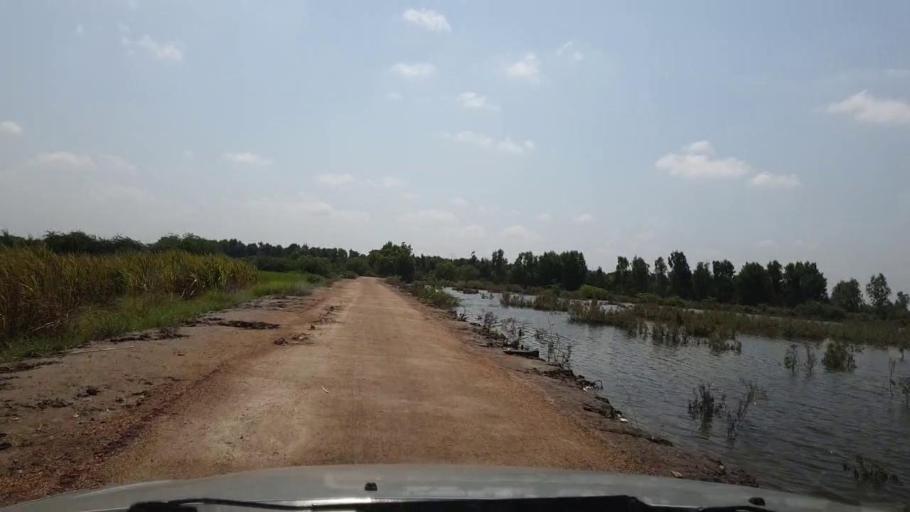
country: PK
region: Sindh
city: Rajo Khanani
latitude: 25.0136
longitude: 68.8567
